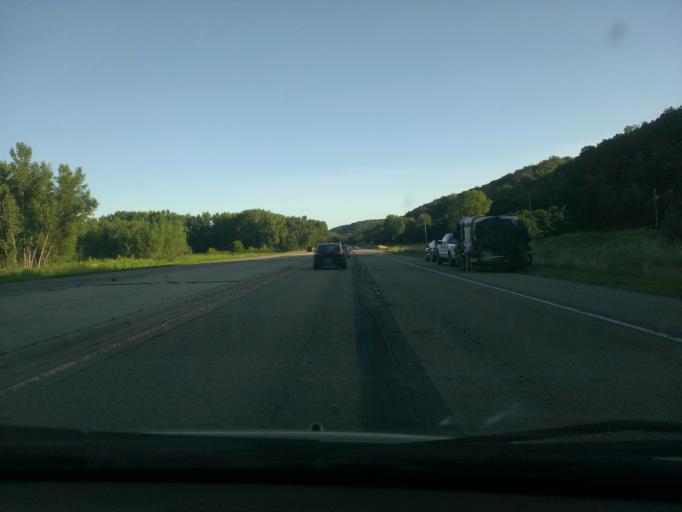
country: US
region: Minnesota
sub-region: Nicollet County
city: North Mankato
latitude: 44.2283
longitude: -94.0274
